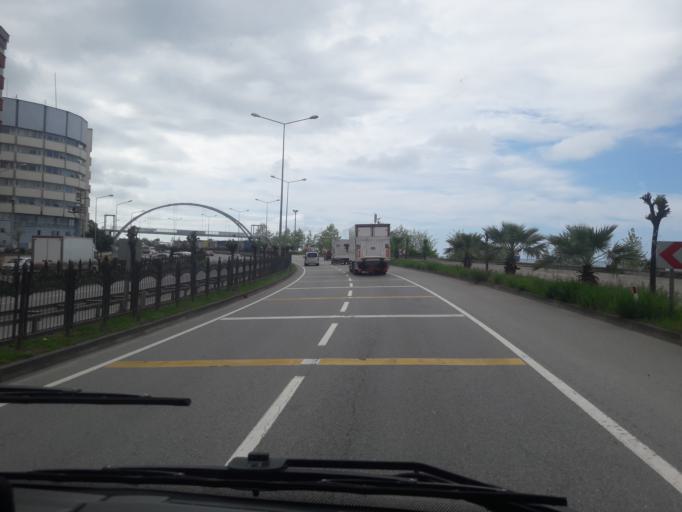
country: TR
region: Giresun
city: Giresun
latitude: 40.9220
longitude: 38.3930
